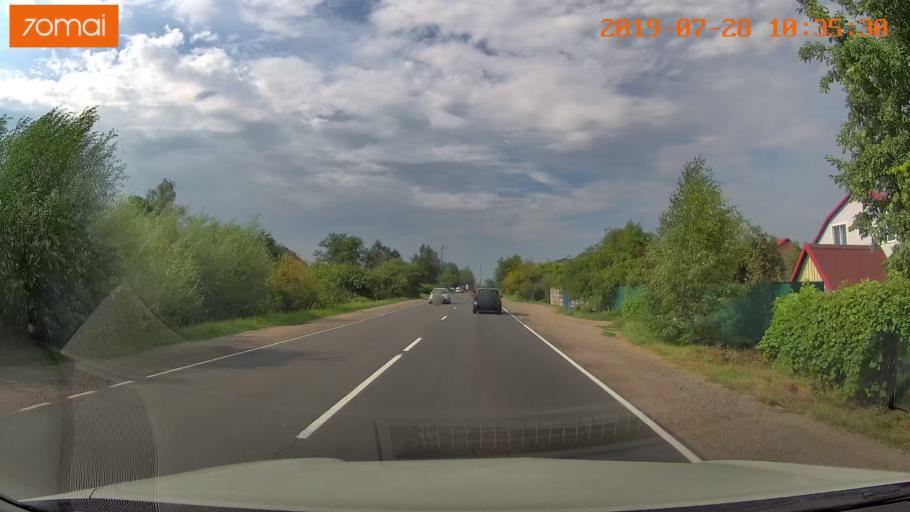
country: RU
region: Kaliningrad
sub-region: Gorod Kaliningrad
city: Kaliningrad
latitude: 54.7461
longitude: 20.4309
